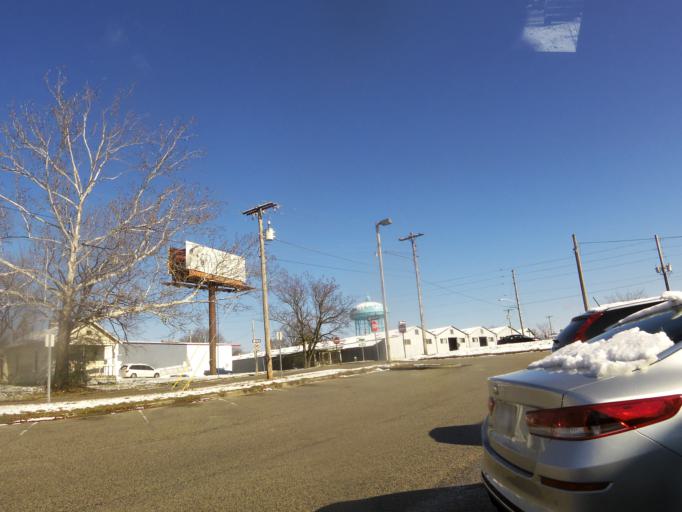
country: US
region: North Carolina
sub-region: Wilson County
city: Wilson
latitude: 35.7217
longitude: -77.9169
